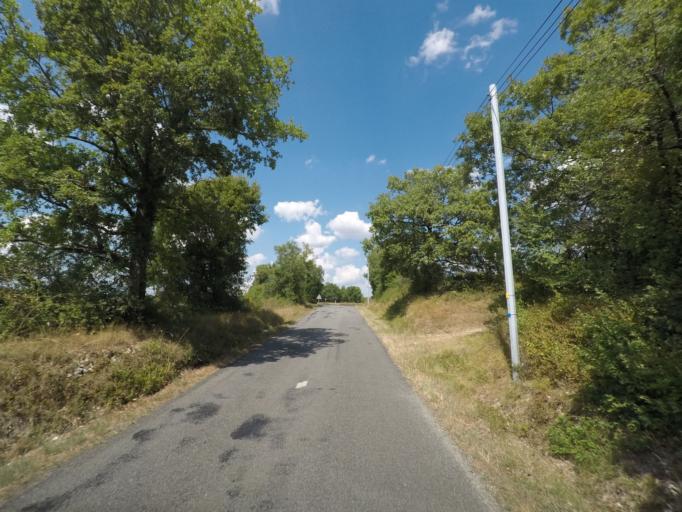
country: FR
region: Midi-Pyrenees
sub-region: Departement du Lot
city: Le Vigan
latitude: 44.6020
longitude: 1.5857
